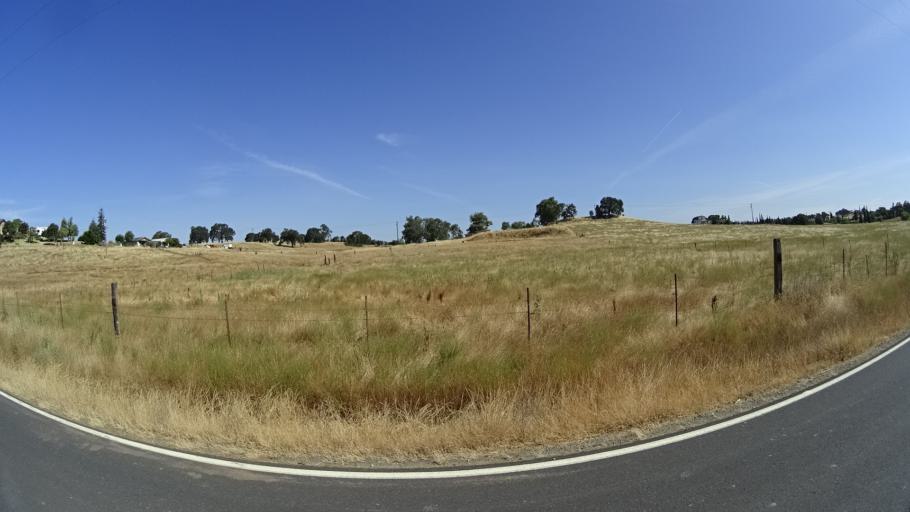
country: US
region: California
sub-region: Calaveras County
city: Rancho Calaveras
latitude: 38.0968
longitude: -120.9039
